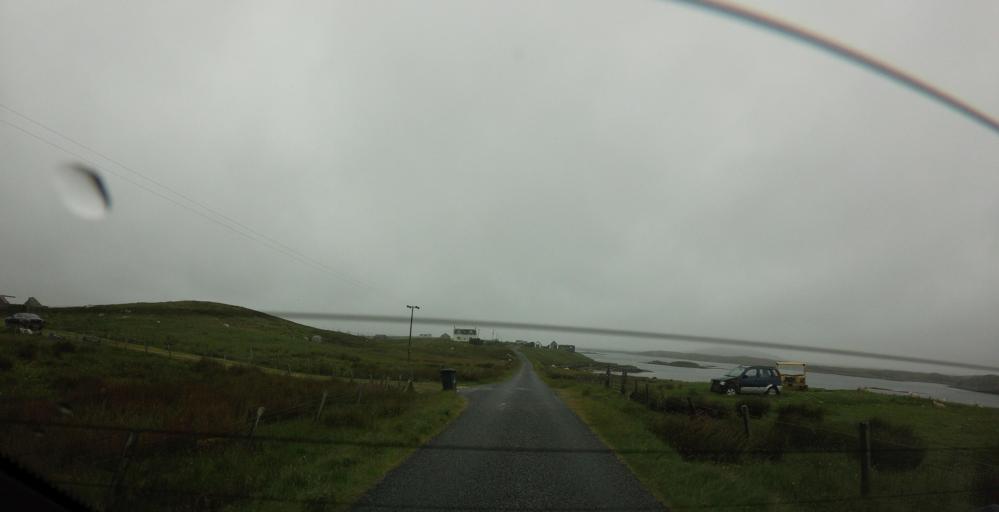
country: GB
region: Scotland
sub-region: Eilean Siar
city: Isle of North Uist
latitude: 57.5507
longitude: -7.2341
